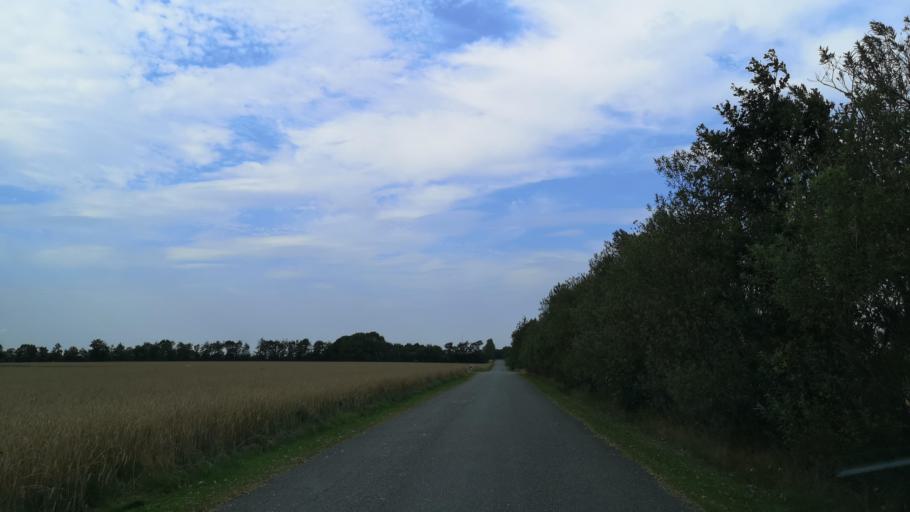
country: DK
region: Central Jutland
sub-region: Ringkobing-Skjern Kommune
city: Videbaek
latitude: 56.0724
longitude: 8.6809
